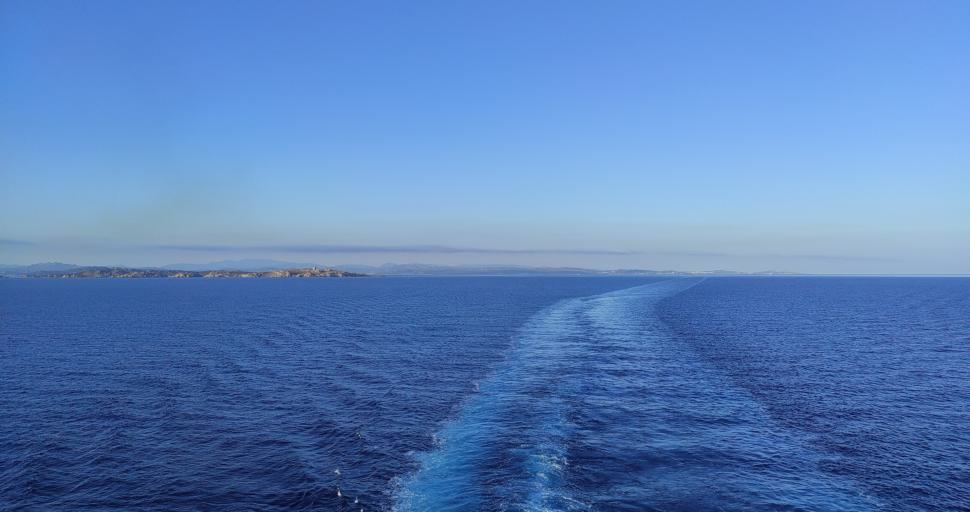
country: IT
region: Sardinia
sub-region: Provincia di Olbia-Tempio
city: La Maddalena
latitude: 41.3495
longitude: 9.3603
